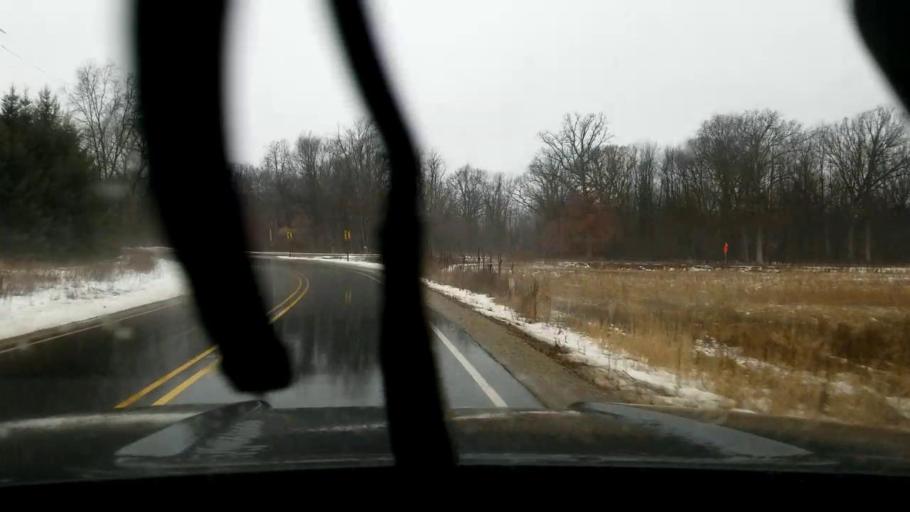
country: US
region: Michigan
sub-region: Jackson County
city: Michigan Center
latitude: 42.3211
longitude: -84.3024
